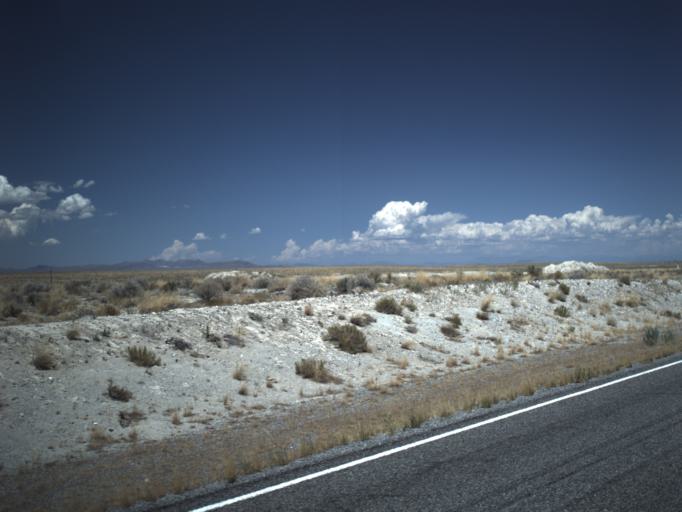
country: US
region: Utah
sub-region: Millard County
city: Delta
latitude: 39.1753
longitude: -113.0263
